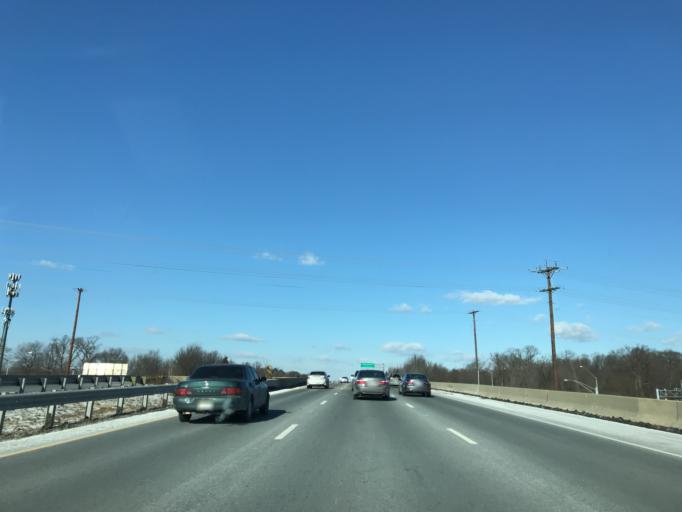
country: US
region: Maryland
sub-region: Prince George's County
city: Camp Springs
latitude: 38.8041
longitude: -76.9052
